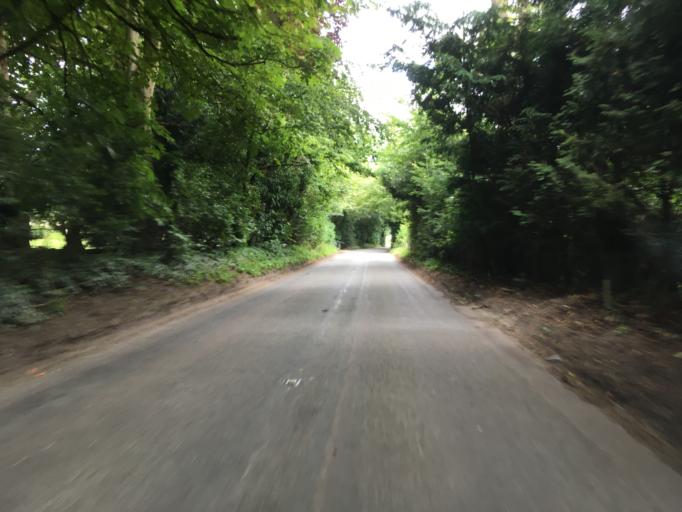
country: GB
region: England
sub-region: West Berkshire
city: Winterbourne
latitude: 51.4202
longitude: -1.3626
